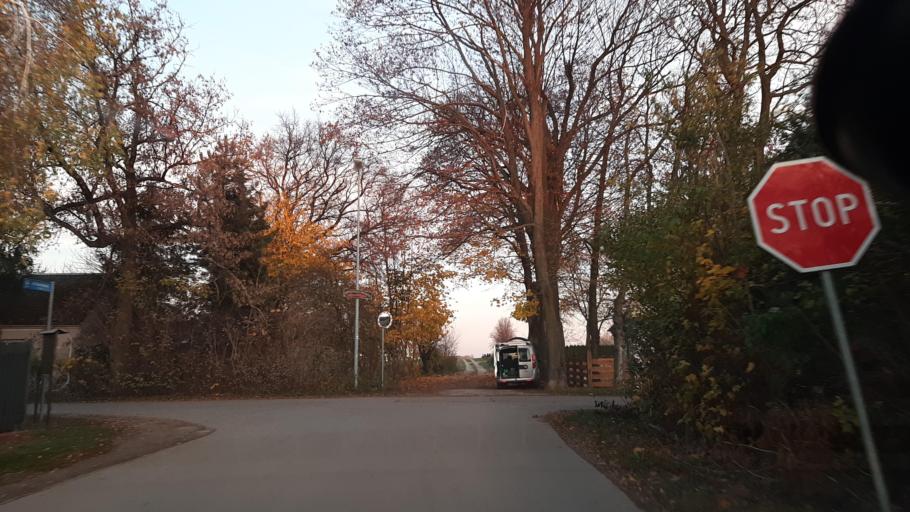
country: PL
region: Lublin Voivodeship
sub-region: Powiat lubelski
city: Jastkow
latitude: 51.2922
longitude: 22.5055
